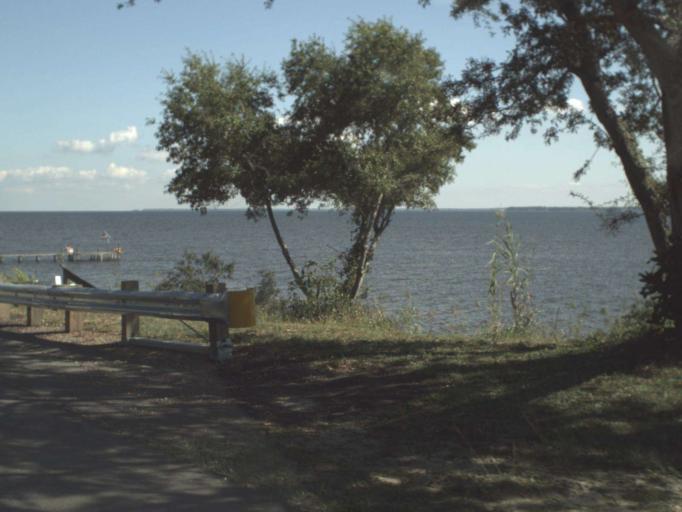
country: US
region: Florida
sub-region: Walton County
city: Miramar Beach
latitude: 30.4650
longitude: -86.3679
